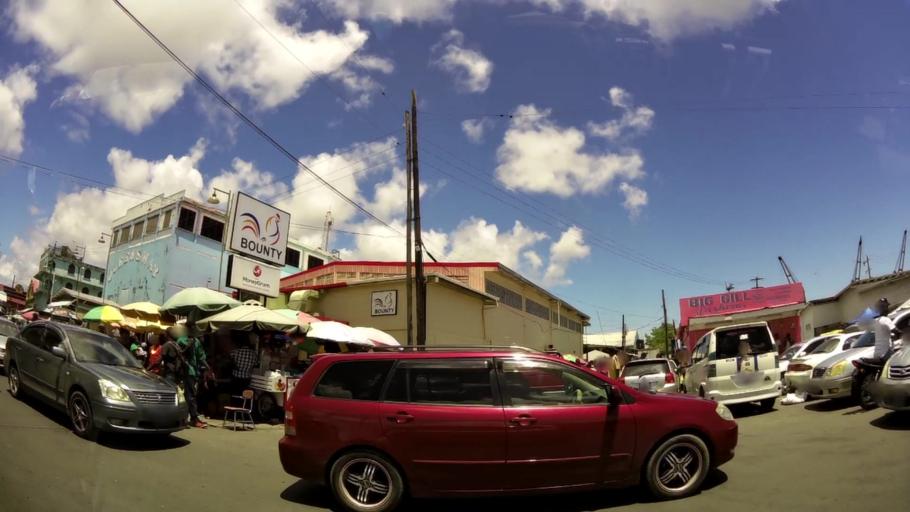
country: GY
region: Demerara-Mahaica
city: Georgetown
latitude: 6.8112
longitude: -58.1666
